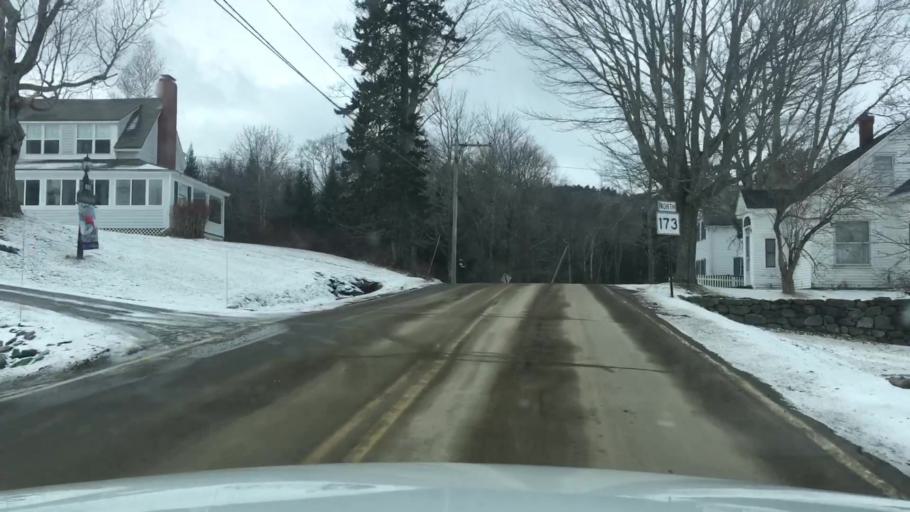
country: US
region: Maine
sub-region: Waldo County
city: Lincolnville
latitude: 44.2816
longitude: -69.0101
